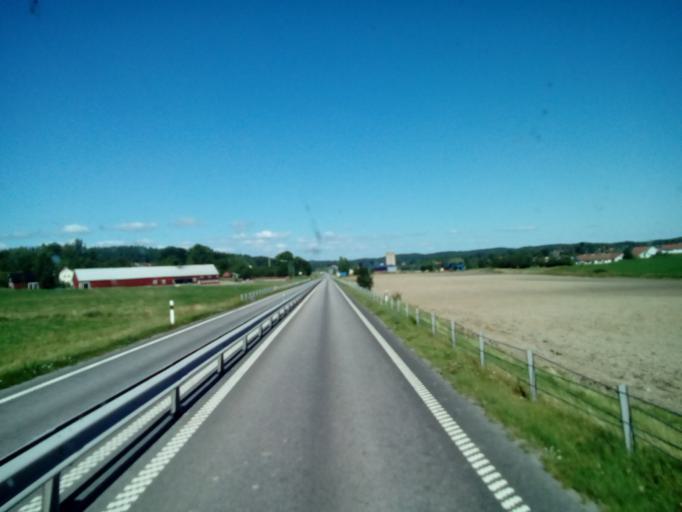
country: SE
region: OEstergoetland
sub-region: Kinda Kommun
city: Rimforsa
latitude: 58.1265
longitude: 15.6737
